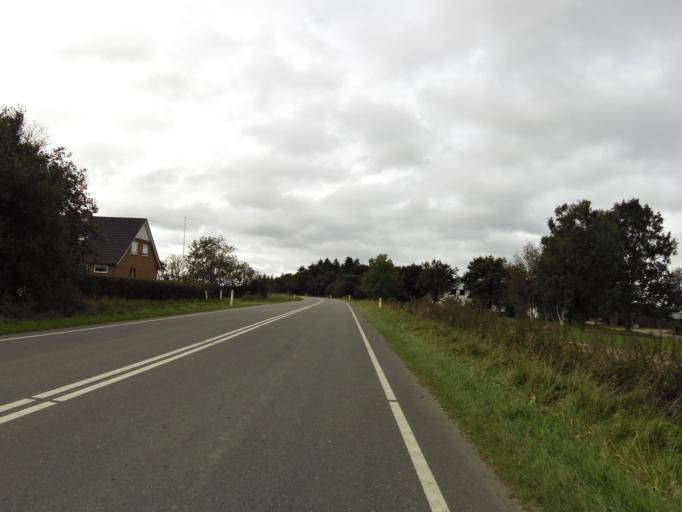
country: DK
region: South Denmark
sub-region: Tonder Kommune
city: Sherrebek
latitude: 55.2005
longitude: 8.7745
